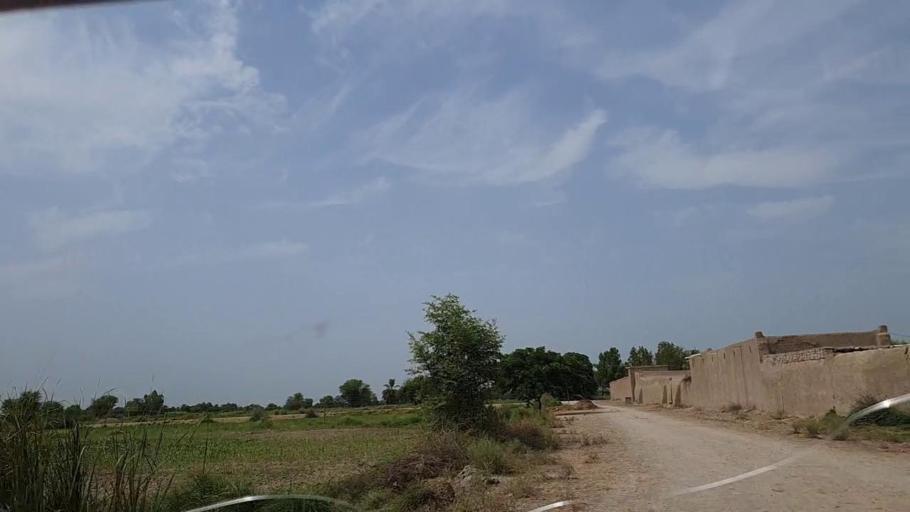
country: PK
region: Sindh
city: Tharu Shah
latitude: 26.9034
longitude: 68.0749
